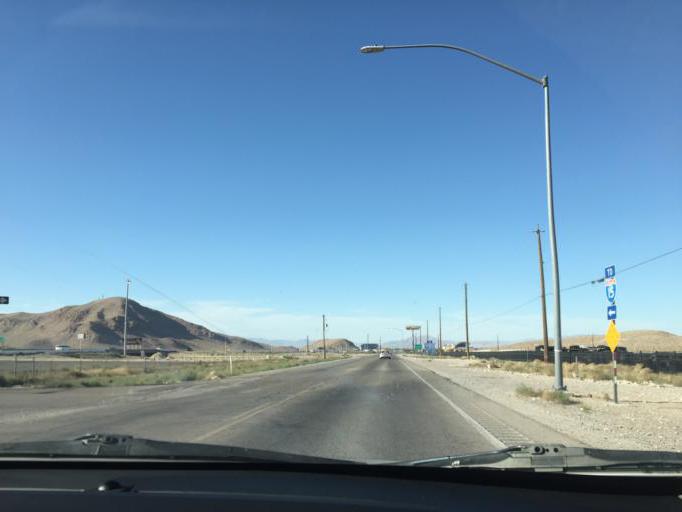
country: US
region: Nevada
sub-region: Clark County
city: Enterprise
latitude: 35.9282
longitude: -115.1932
